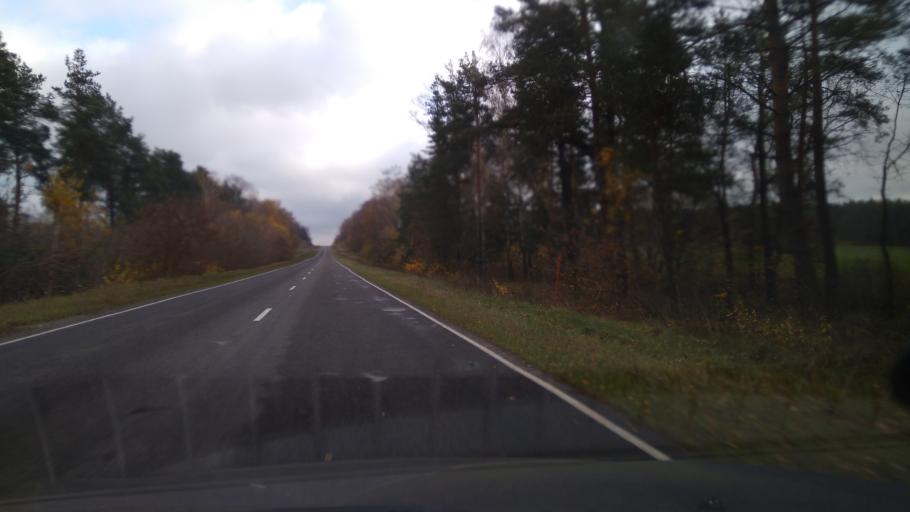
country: BY
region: Minsk
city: Urechcha
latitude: 53.2101
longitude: 27.9922
